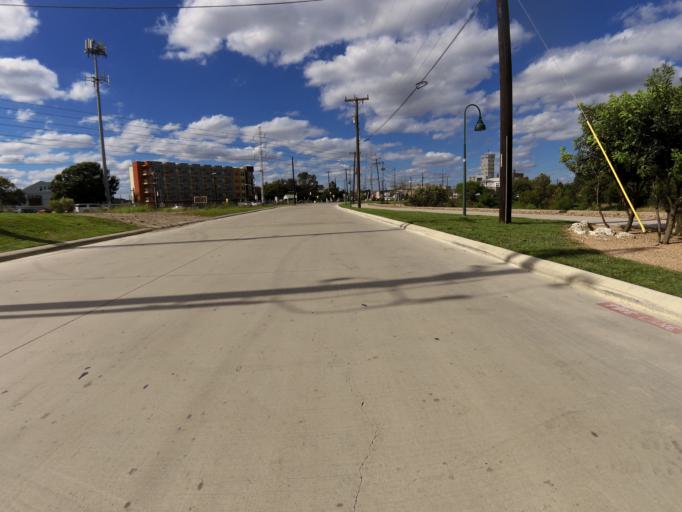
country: US
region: Texas
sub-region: Bexar County
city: San Antonio
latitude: 29.4066
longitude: -98.4942
